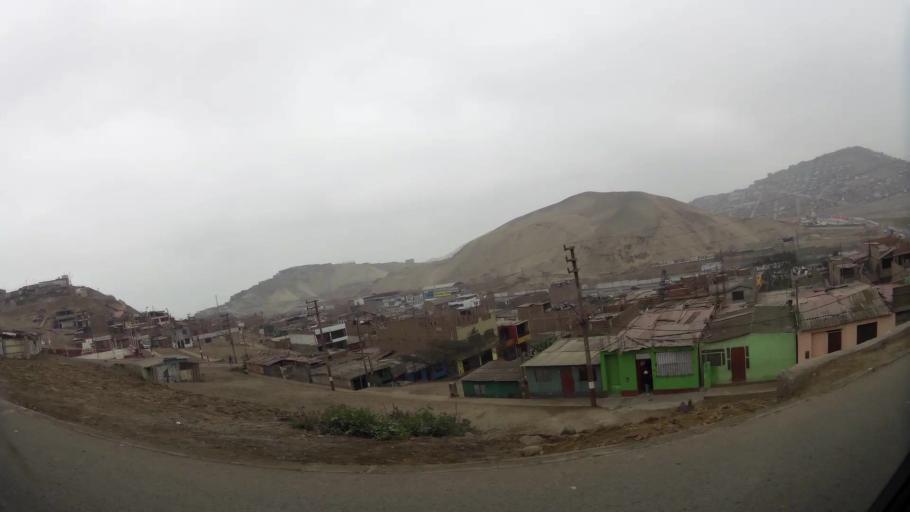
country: PE
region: Lima
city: Ventanilla
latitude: -11.8439
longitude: -77.1144
